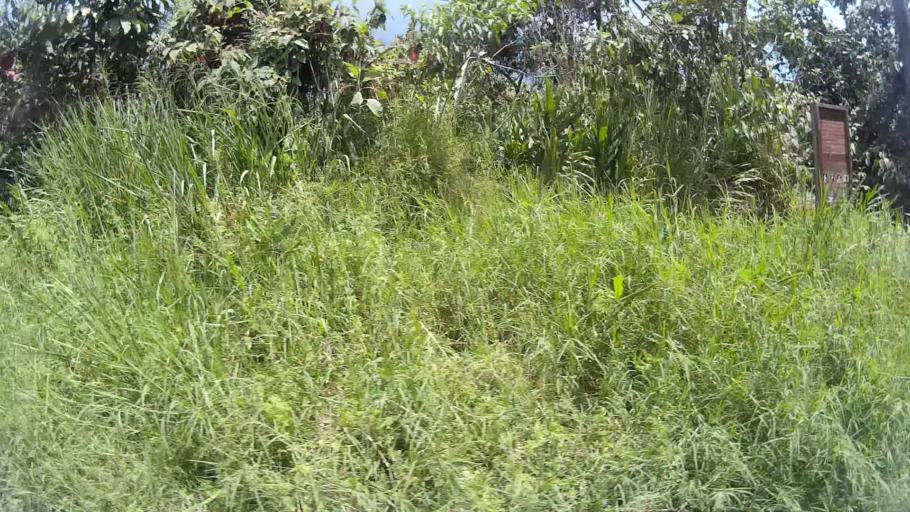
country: CO
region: Quindio
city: Filandia
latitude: 4.7161
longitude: -75.6739
